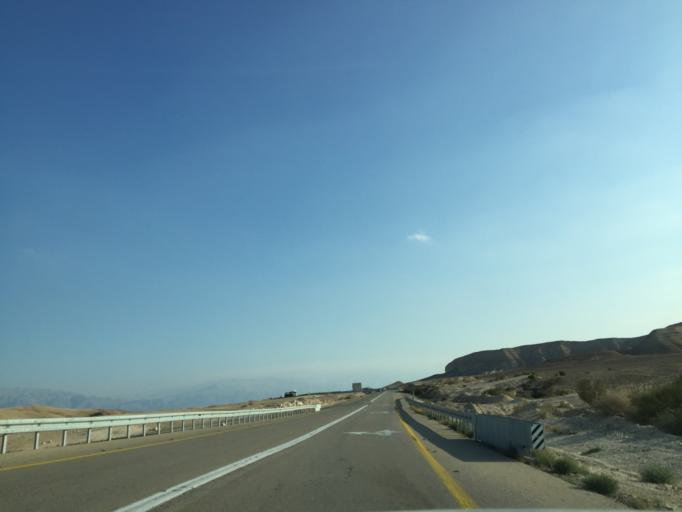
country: IL
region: Southern District
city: `En Boqeq
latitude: 31.1706
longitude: 35.3153
